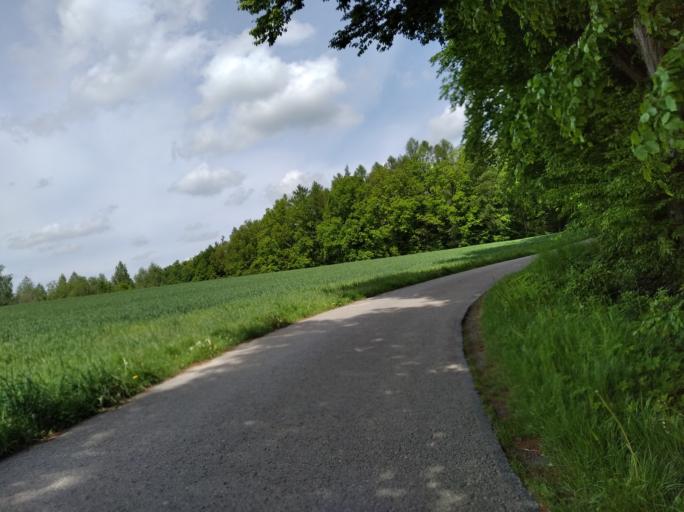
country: PL
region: Subcarpathian Voivodeship
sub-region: Powiat strzyzowski
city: Czudec
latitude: 49.9283
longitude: 21.8292
